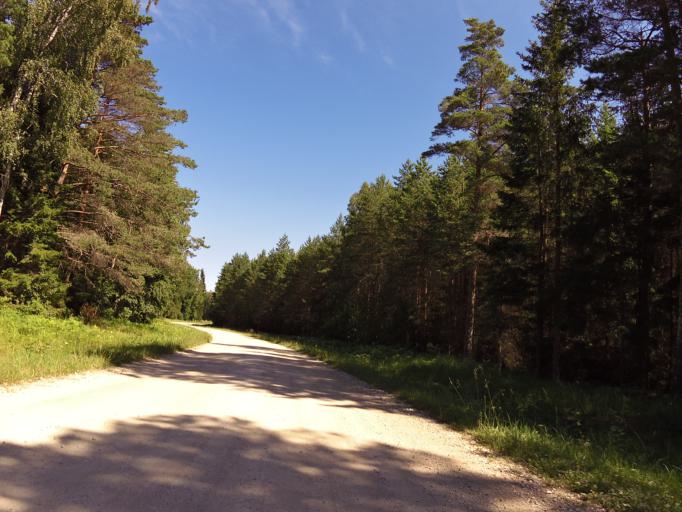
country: EE
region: Hiiumaa
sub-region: Kaerdla linn
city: Kardla
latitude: 58.9220
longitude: 22.3654
